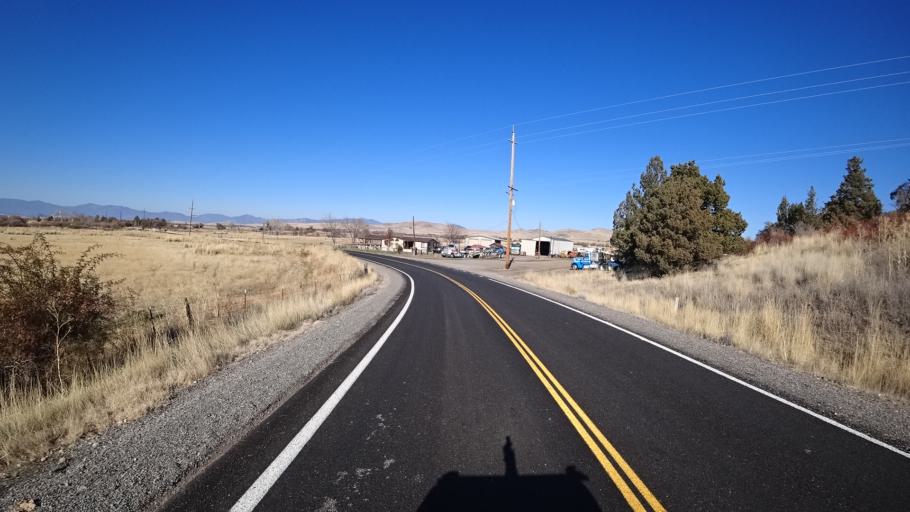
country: US
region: California
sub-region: Siskiyou County
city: Montague
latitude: 41.7109
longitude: -122.3797
